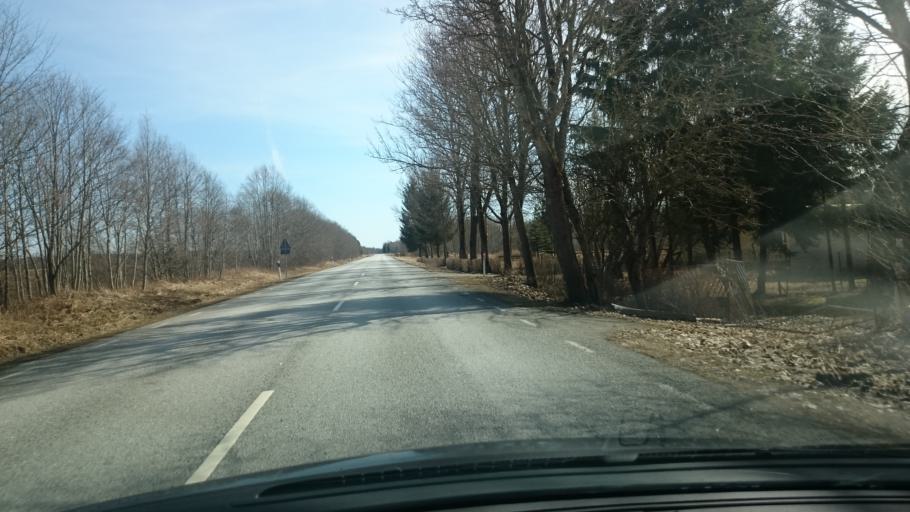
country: EE
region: Paernumaa
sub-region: Tootsi vald
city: Tootsi
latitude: 58.6571
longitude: 24.8354
